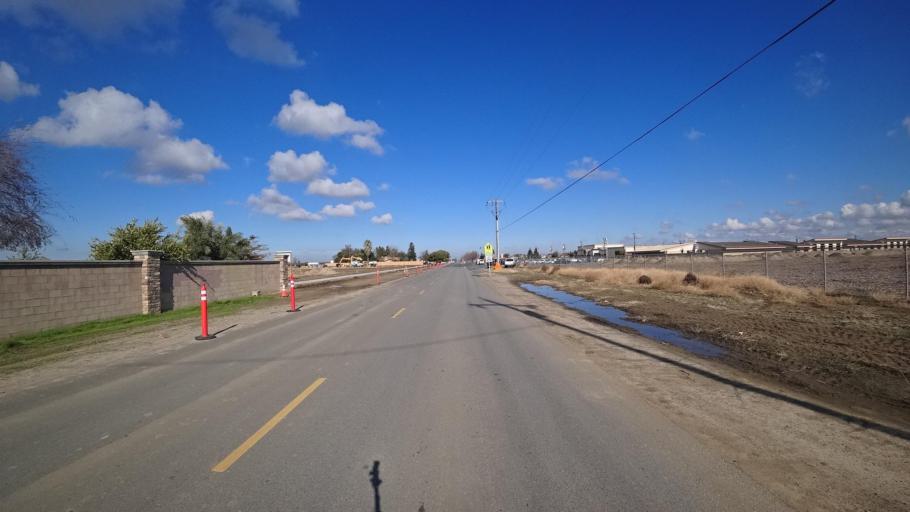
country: US
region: California
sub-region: Kern County
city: McFarland
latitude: 35.6650
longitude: -119.2412
